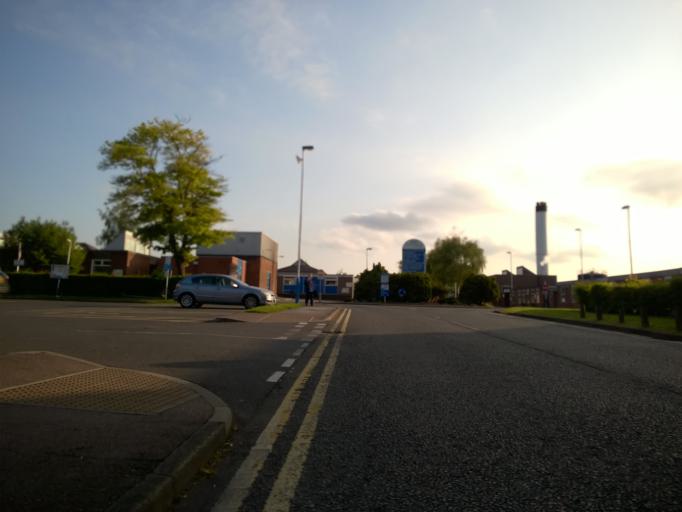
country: GB
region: England
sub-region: Leicestershire
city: Oadby
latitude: 52.6313
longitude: -1.0820
